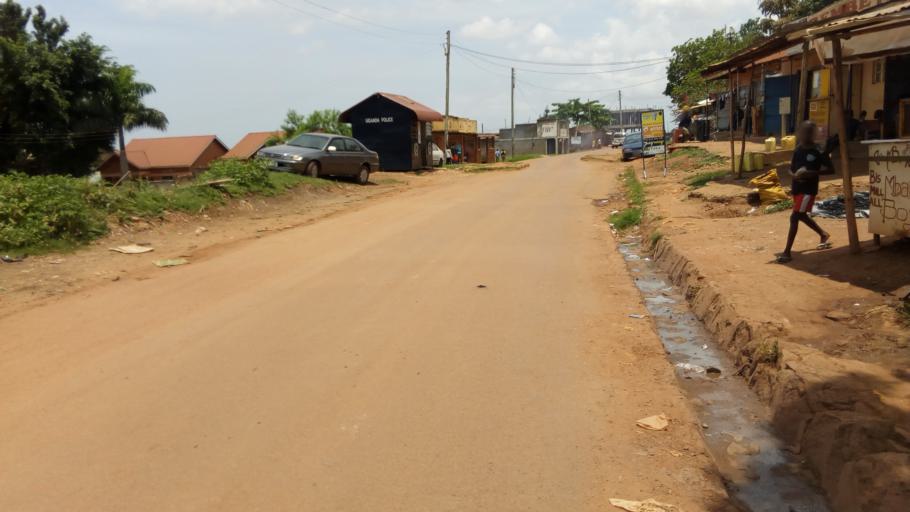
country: UG
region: Central Region
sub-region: Wakiso District
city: Kireka
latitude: 0.3236
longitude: 32.6349
